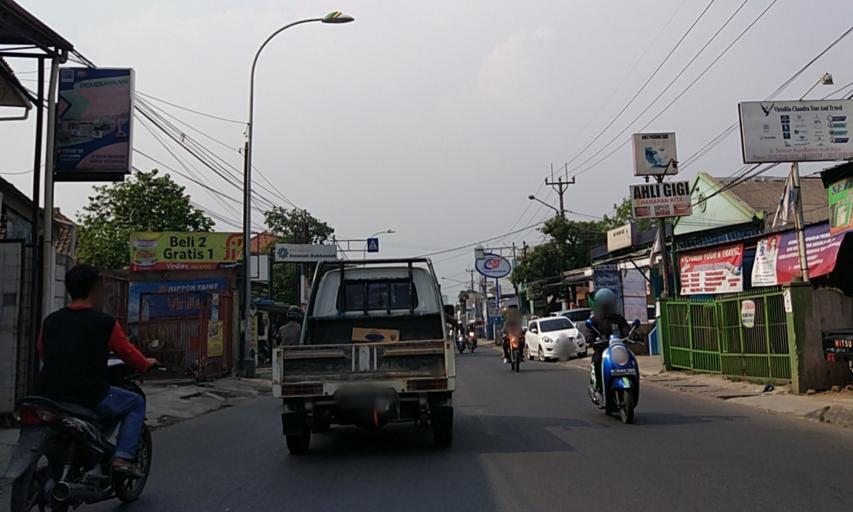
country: ID
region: West Java
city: Margahayukencana
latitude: -6.9866
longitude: 107.5597
